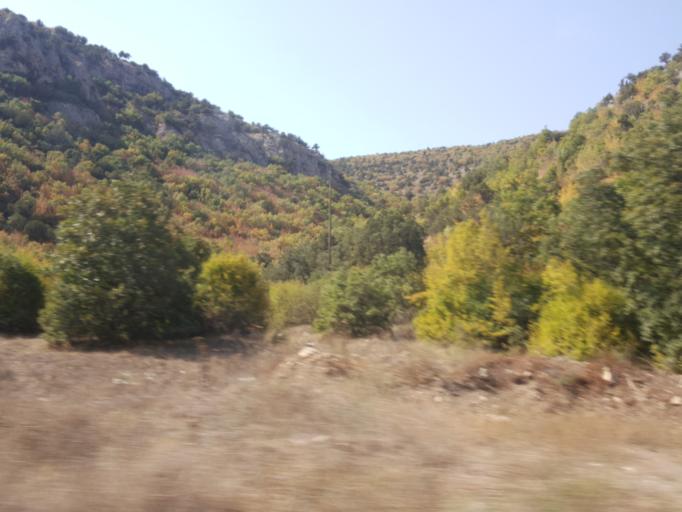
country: TR
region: Yozgat
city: Cekerek
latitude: 40.1165
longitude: 35.6126
